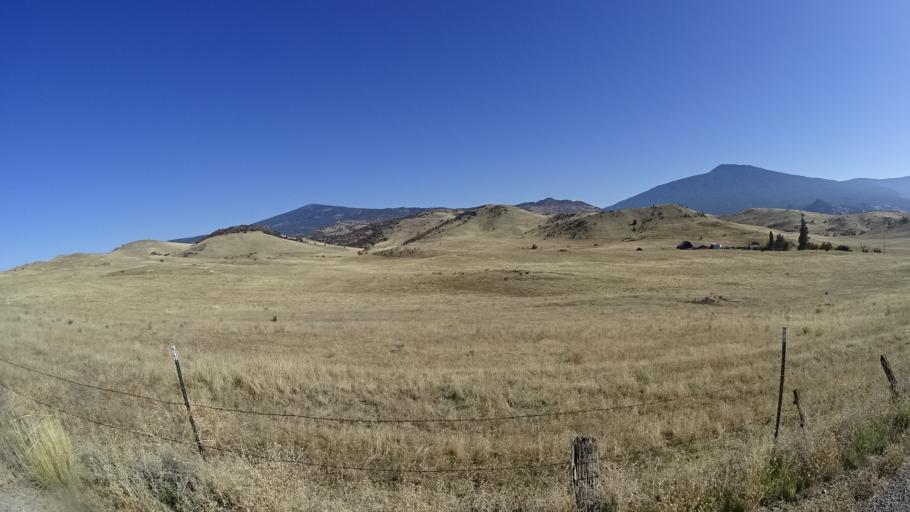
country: US
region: California
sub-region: Siskiyou County
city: Montague
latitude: 41.7664
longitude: -122.3571
